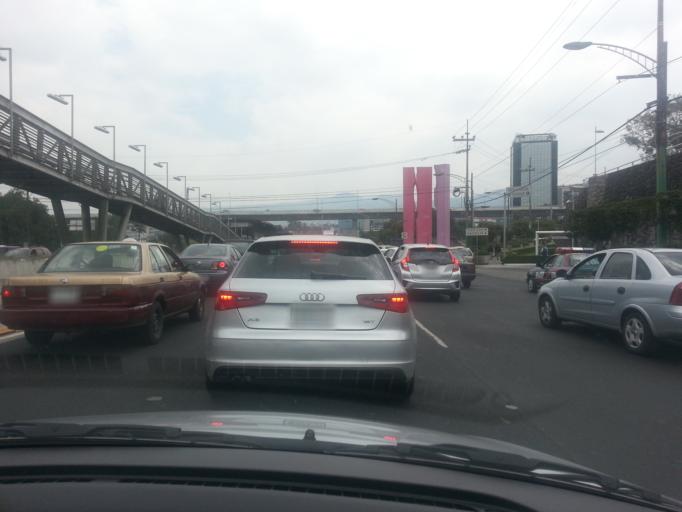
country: MX
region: Mexico City
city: Tlalpan
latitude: 19.3051
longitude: -99.1863
